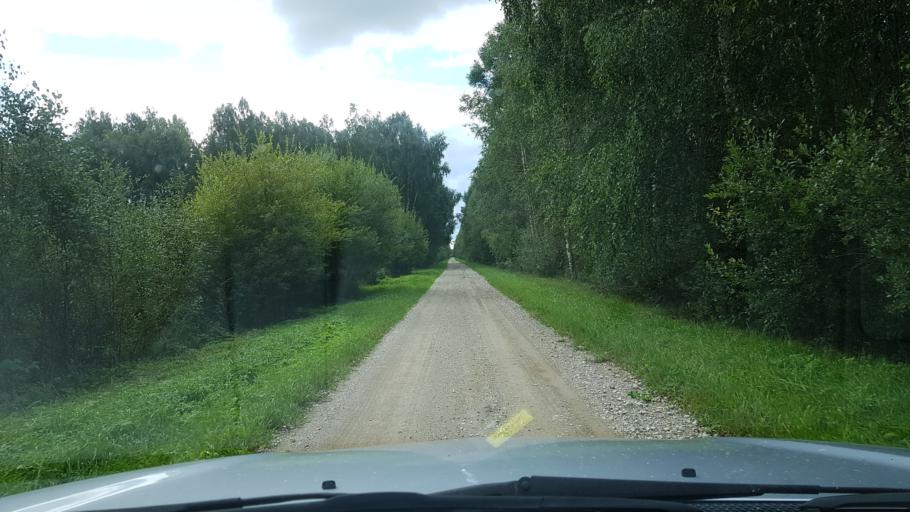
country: EE
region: Harju
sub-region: Raasiku vald
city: Arukula
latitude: 59.2838
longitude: 25.0520
